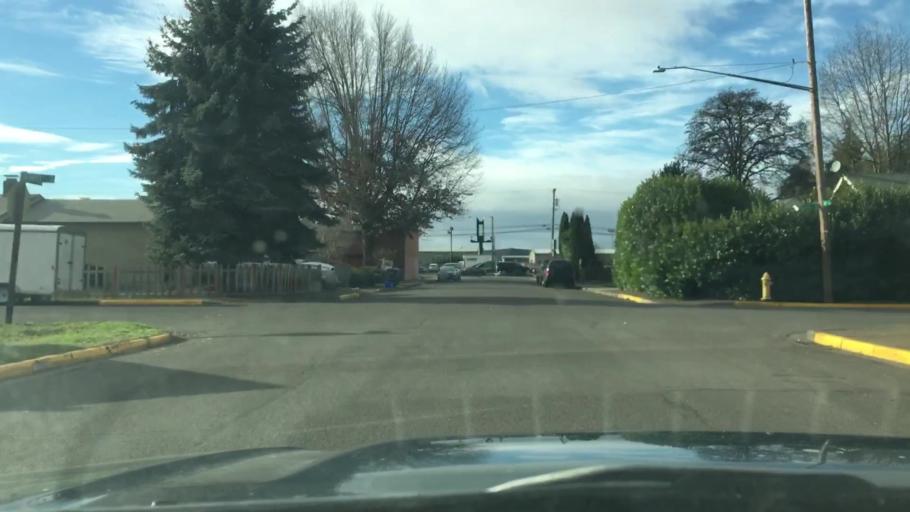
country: US
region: Oregon
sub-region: Lane County
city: Eugene
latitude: 44.0493
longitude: -123.1214
